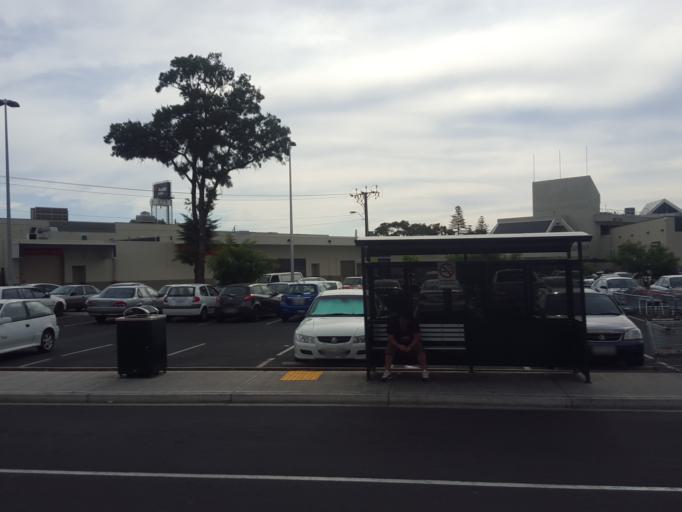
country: AU
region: South Australia
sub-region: Charles Sturt
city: Woodville North
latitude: -34.8742
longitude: 138.5511
